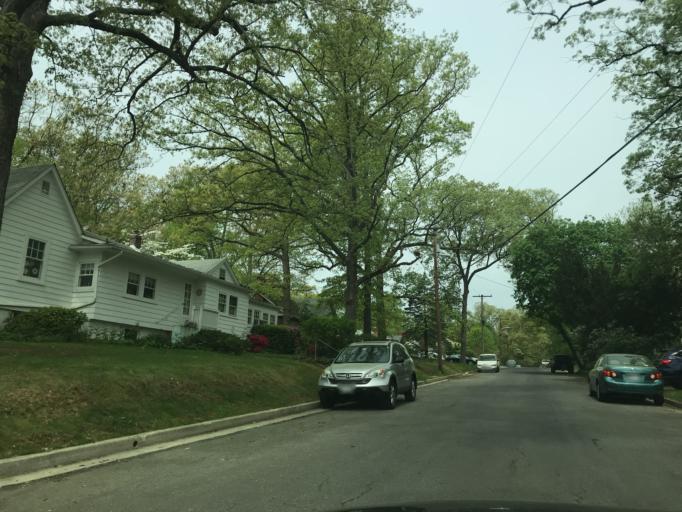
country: US
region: Maryland
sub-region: Baltimore County
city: Catonsville
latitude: 39.2630
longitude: -76.7352
